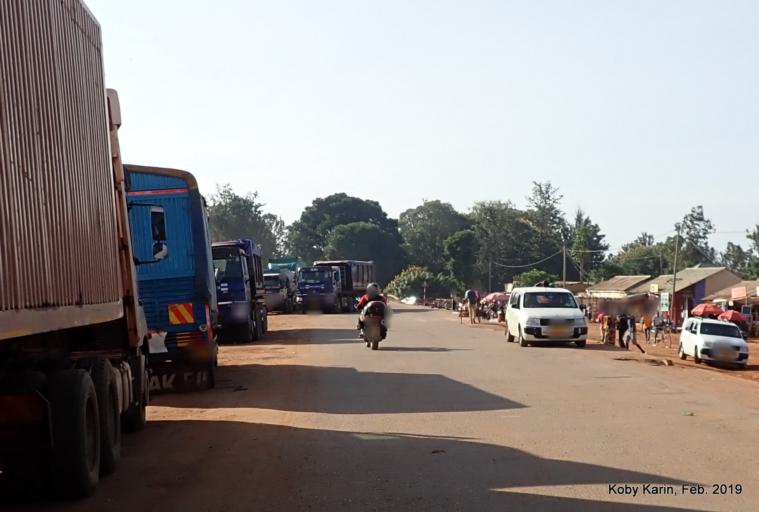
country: TZ
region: Kagera
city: Biharamulo
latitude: -2.7657
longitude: 30.9967
